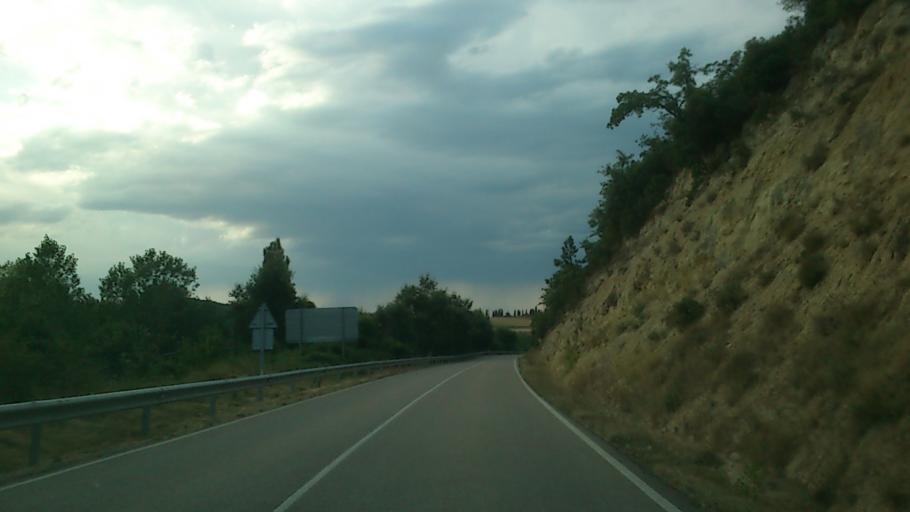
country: ES
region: Castille and Leon
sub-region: Provincia de Burgos
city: Trespaderne
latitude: 42.7936
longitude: -3.3749
